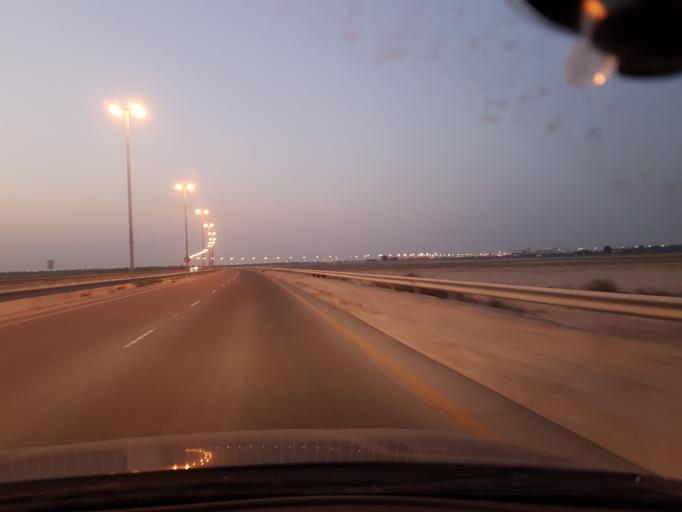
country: BH
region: Central Governorate
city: Dar Kulayb
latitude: 26.0040
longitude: 50.4852
